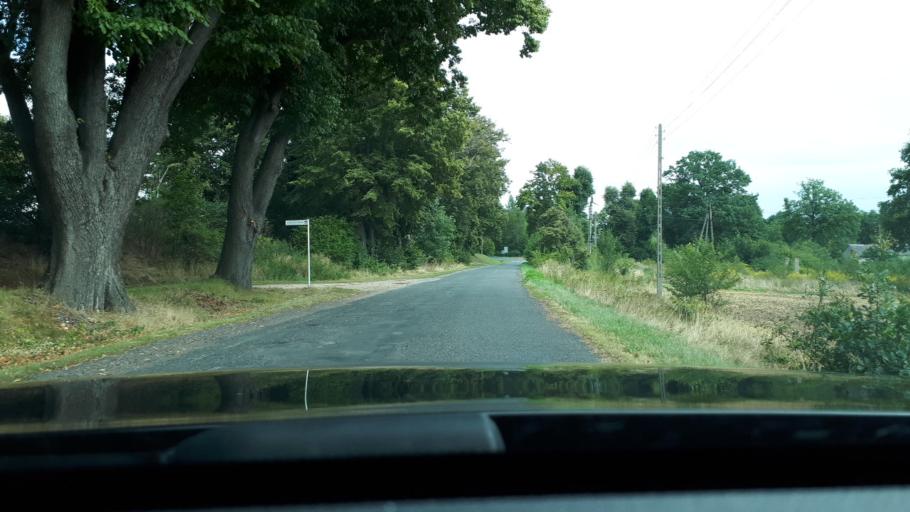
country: PL
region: Lower Silesian Voivodeship
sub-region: Powiat zlotoryjski
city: Olszanica
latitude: 51.2387
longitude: 15.8190
